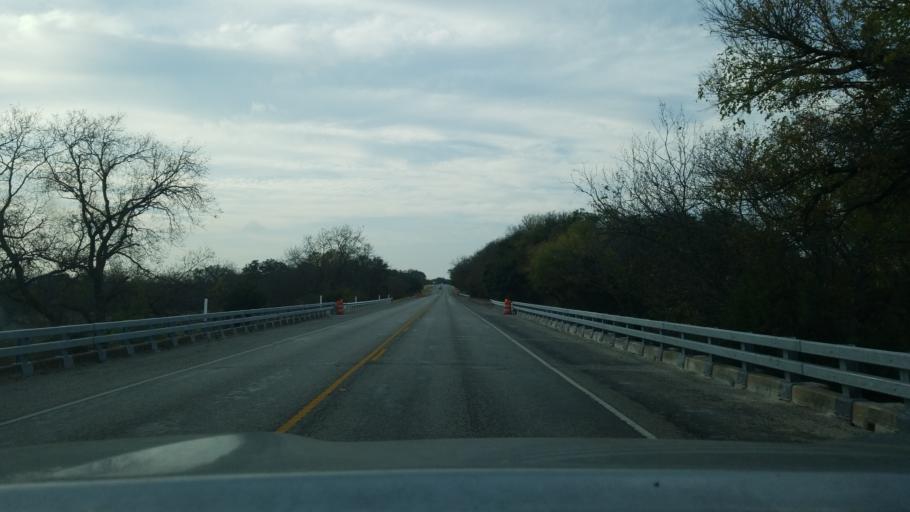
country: US
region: Texas
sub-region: Mills County
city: Goldthwaite
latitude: 31.5506
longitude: -98.6457
